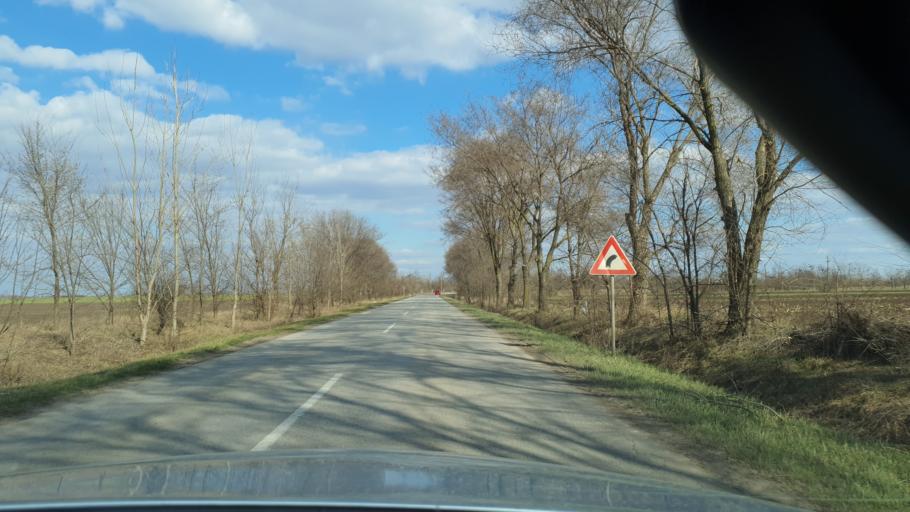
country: RS
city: Ravno Selo
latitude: 45.4580
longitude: 19.6552
